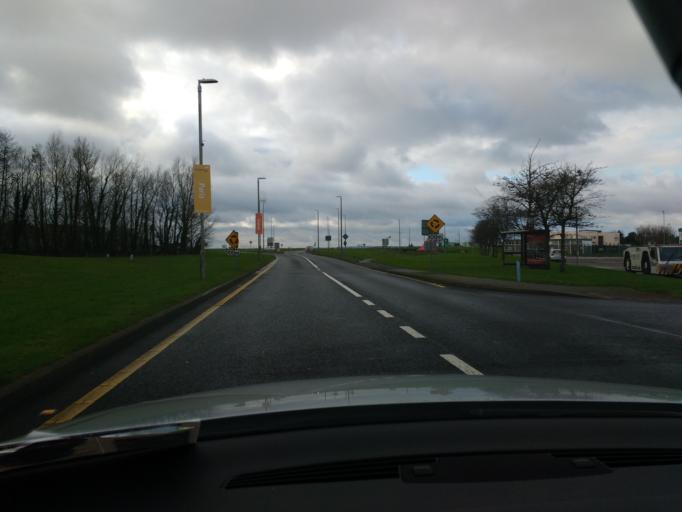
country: IE
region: Munster
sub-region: An Clar
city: Shannon
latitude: 52.6900
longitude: -8.9124
